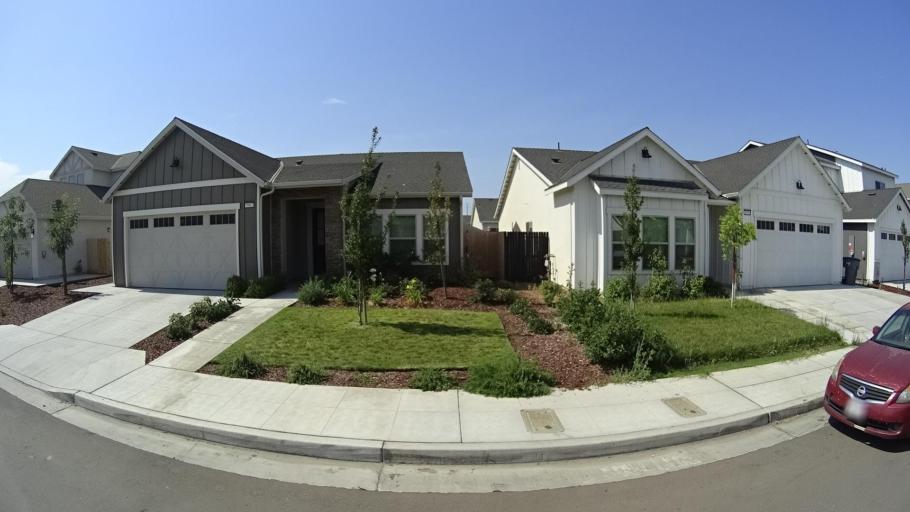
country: US
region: California
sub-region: Fresno County
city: Sunnyside
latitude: 36.7182
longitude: -119.6834
